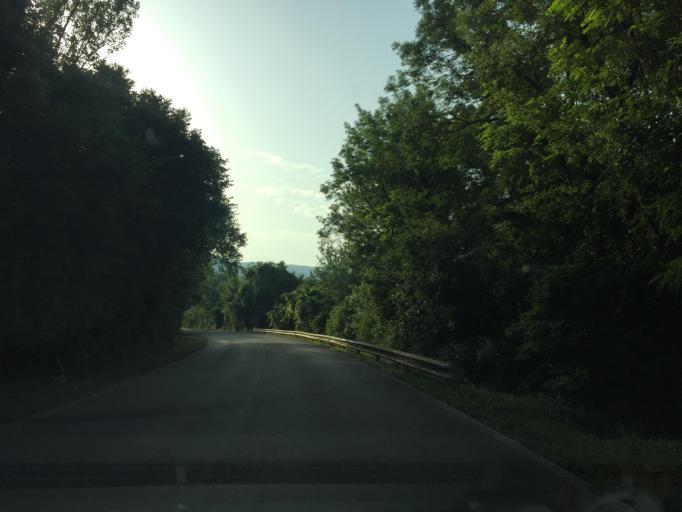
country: IT
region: Friuli Venezia Giulia
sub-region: Provincia di Trieste
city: Domio
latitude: 45.5881
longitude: 13.8205
